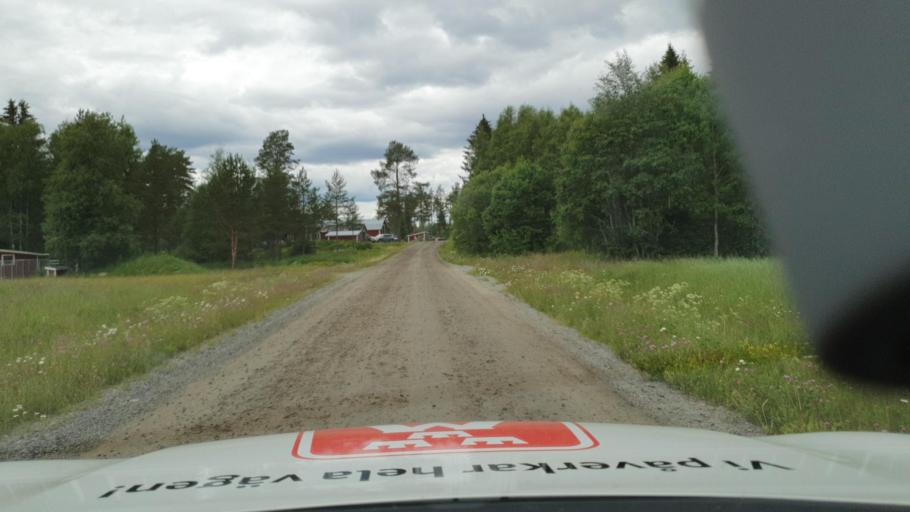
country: SE
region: Vaesterbotten
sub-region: Bjurholms Kommun
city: Bjurholm
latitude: 63.7951
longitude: 19.0912
